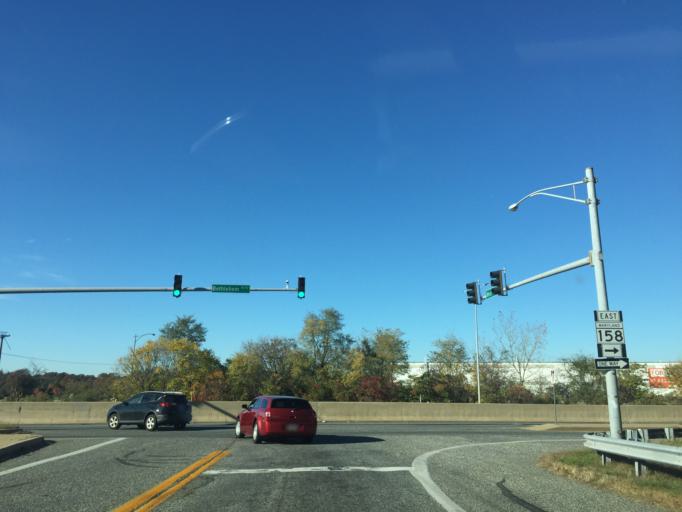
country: US
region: Maryland
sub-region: Baltimore County
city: Edgemere
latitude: 39.2374
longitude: -76.4653
